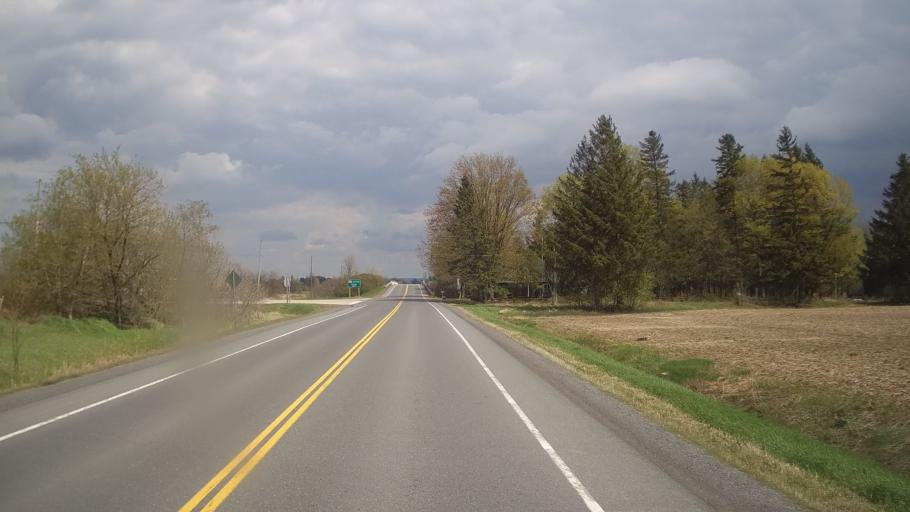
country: CA
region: Ontario
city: Hawkesbury
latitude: 45.5179
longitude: -74.5683
